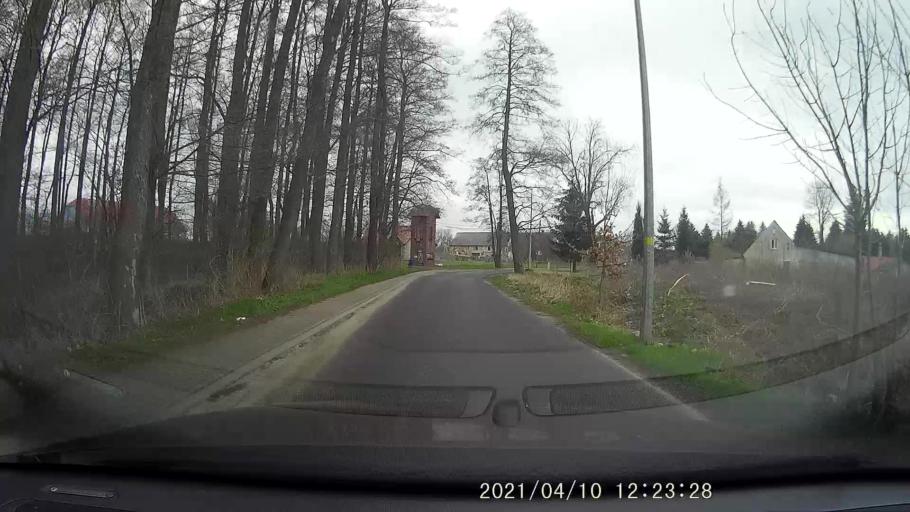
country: PL
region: Lower Silesian Voivodeship
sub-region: Powiat zgorzelecki
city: Zgorzelec
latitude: 51.1634
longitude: 15.0225
